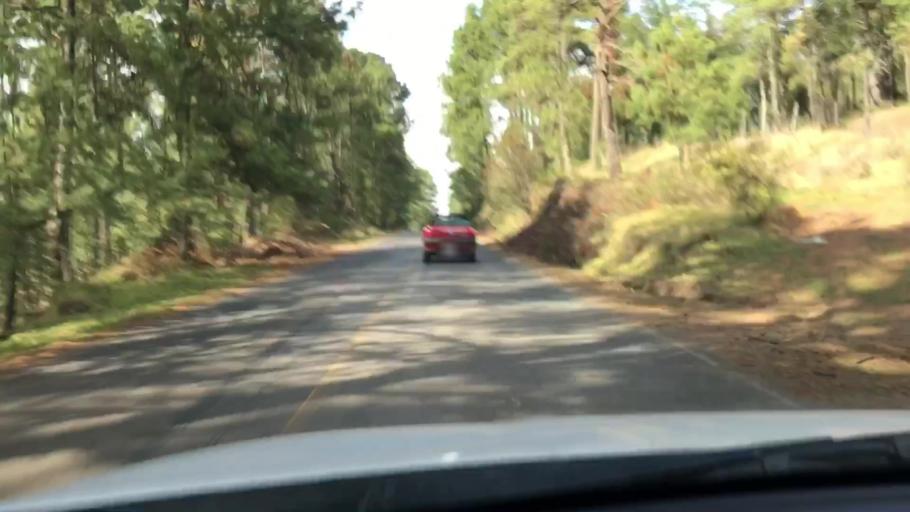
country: MX
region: Jalisco
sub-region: Amacueca
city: Tepec
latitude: 20.0549
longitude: -103.6992
